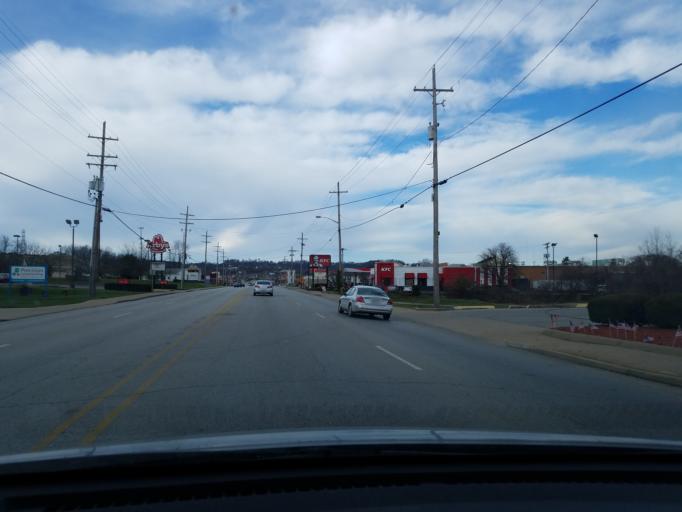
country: US
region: Indiana
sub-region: Floyd County
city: New Albany
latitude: 38.3026
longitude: -85.8371
